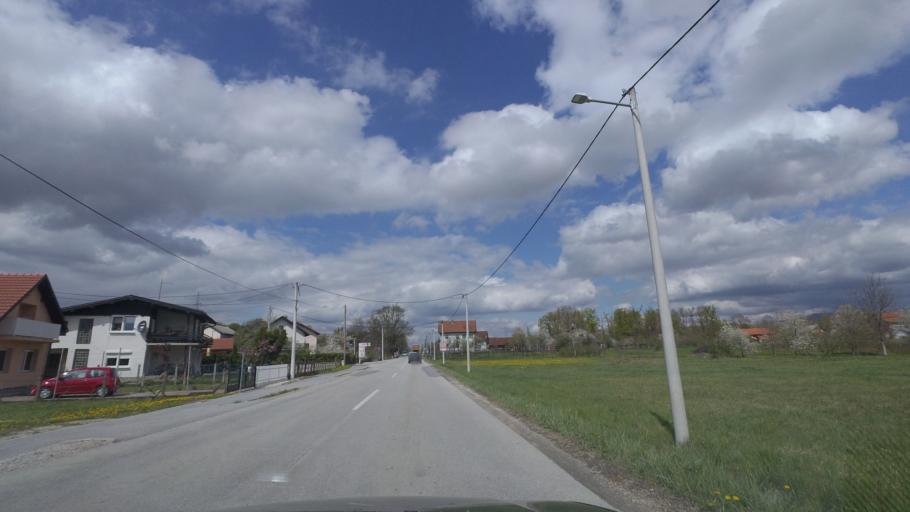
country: HR
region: Zagrebacka
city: Kerestinec
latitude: 45.7549
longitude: 15.8087
